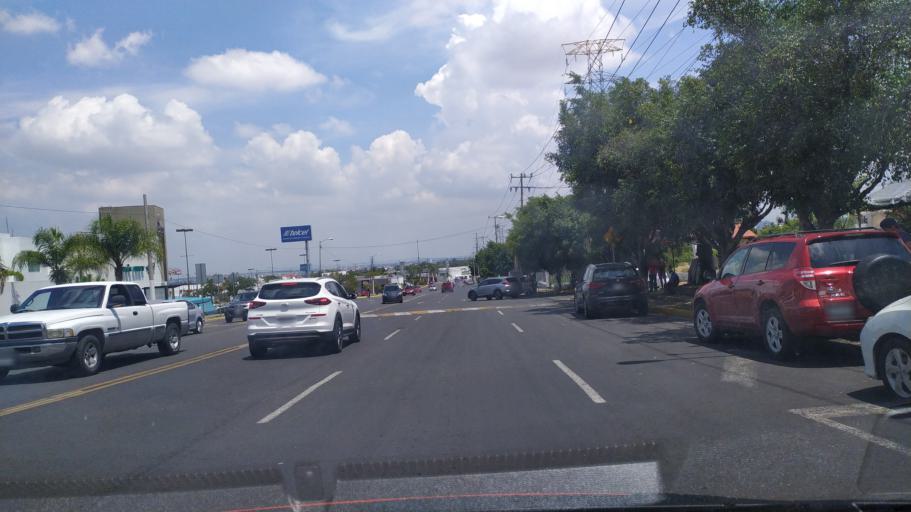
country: MX
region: Jalisco
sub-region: Zapopan
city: Zapopan
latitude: 20.7555
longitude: -103.3861
